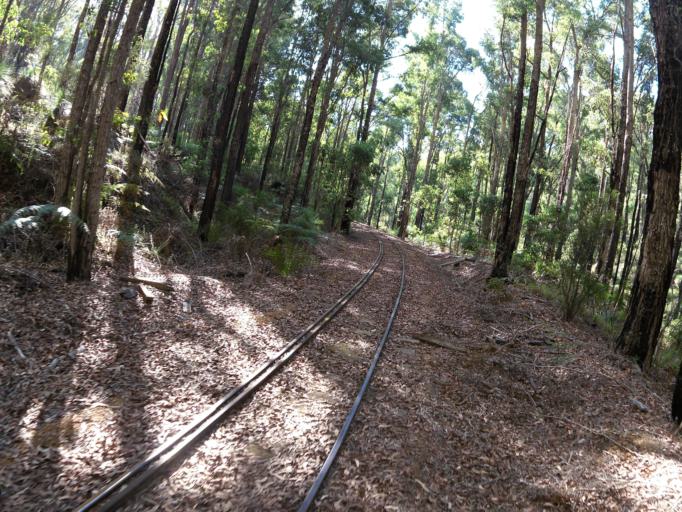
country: AU
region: Western Australia
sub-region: Waroona
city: Waroona
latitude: -32.7279
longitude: 116.1119
